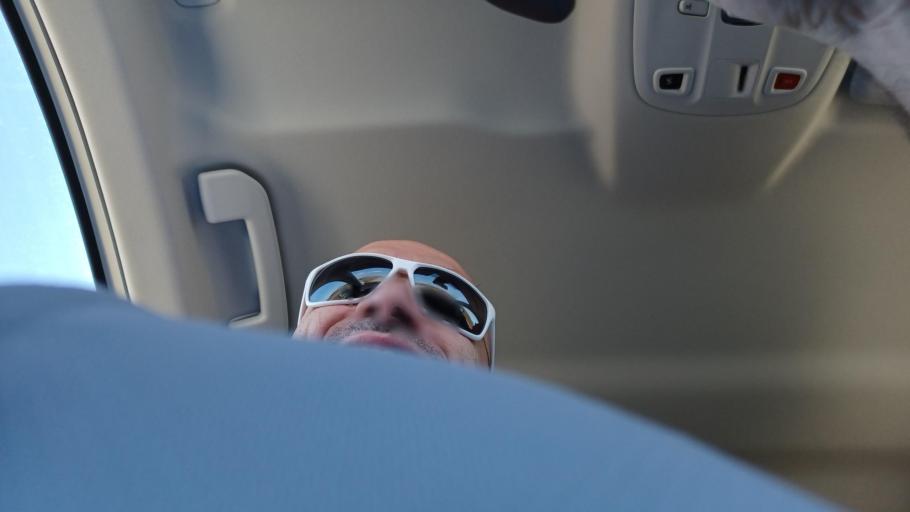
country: ES
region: Catalonia
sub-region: Provincia de Tarragona
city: Camarles
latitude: 40.7735
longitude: 0.6945
